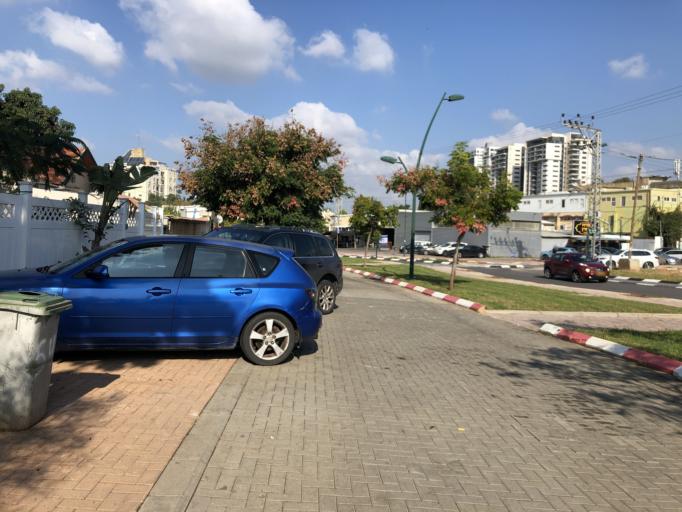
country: IL
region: Tel Aviv
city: Ramat HaSharon
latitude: 32.1280
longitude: 34.8563
